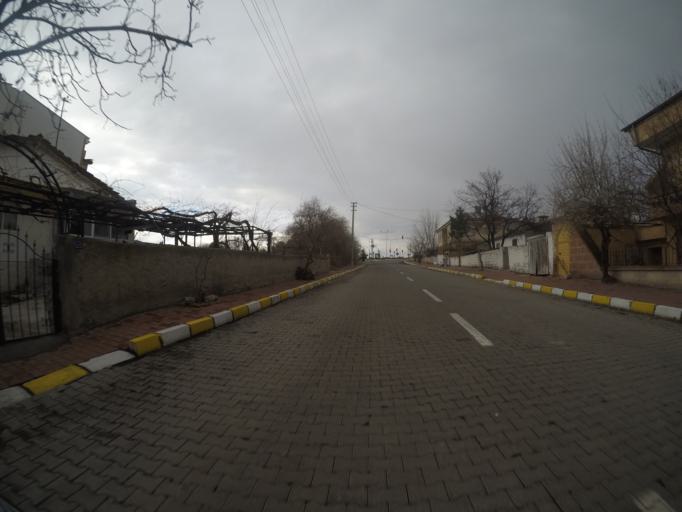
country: TR
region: Nevsehir
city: Goereme
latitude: 38.6303
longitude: 34.8582
